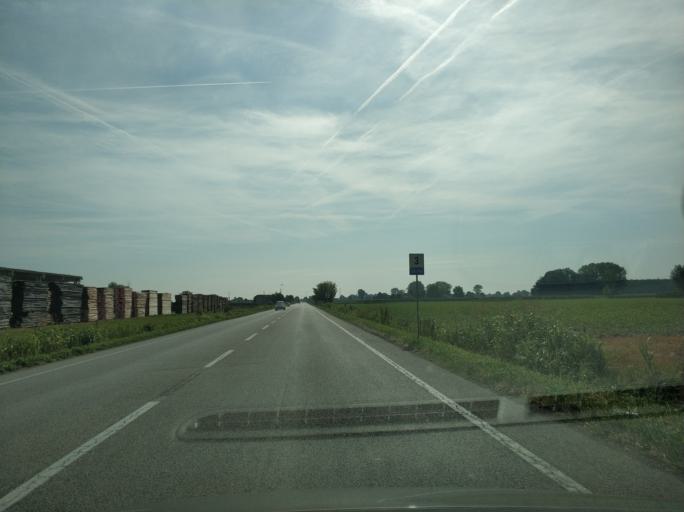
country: IT
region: Veneto
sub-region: Provincia di Padova
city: Pozzonovo
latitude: 45.2105
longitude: 11.7925
